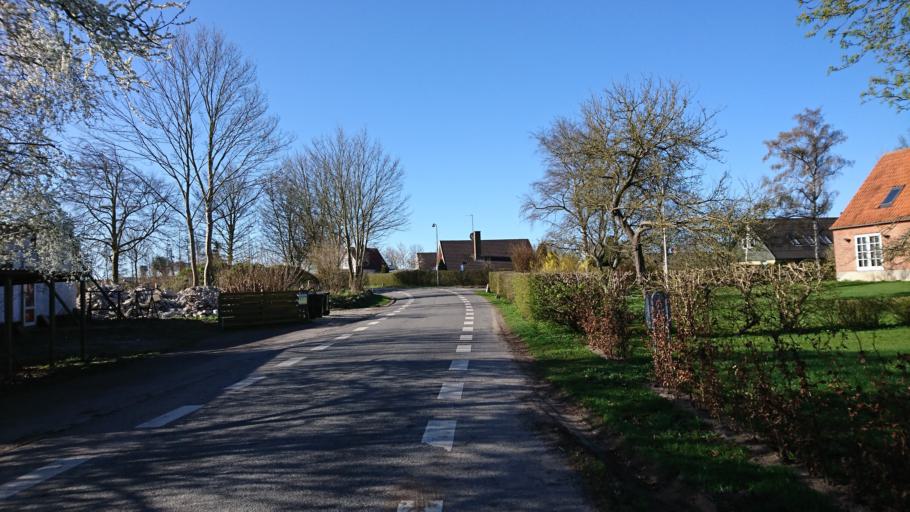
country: DK
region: Capital Region
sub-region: Frederikssund Kommune
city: Skibby
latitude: 55.7225
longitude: 11.9296
